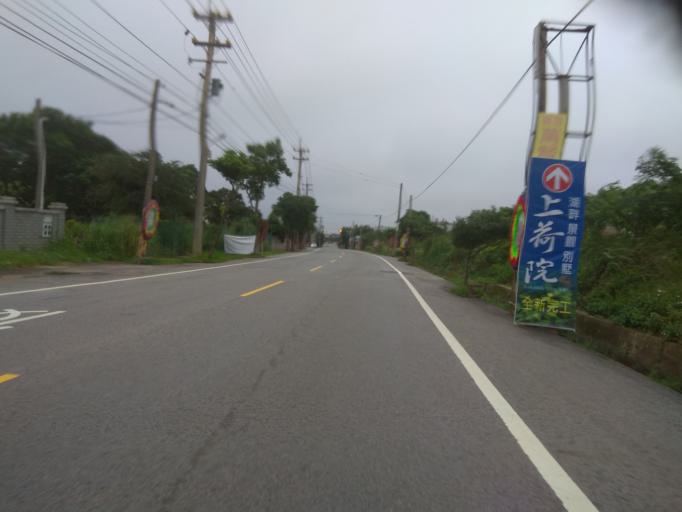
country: TW
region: Taiwan
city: Taoyuan City
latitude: 24.9969
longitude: 121.1170
